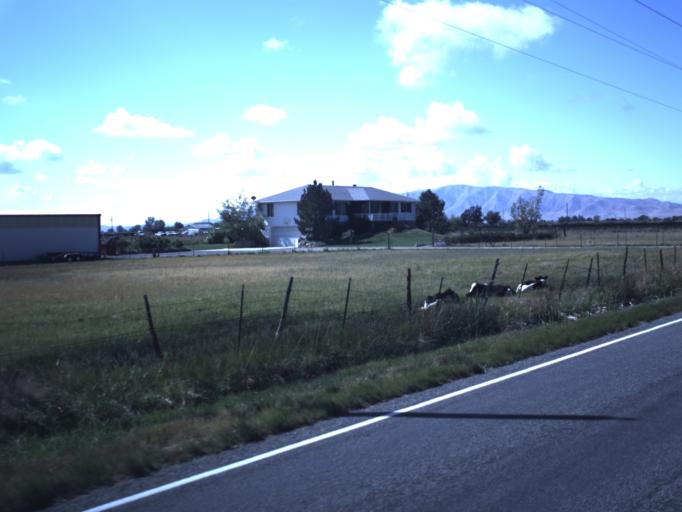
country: US
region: Utah
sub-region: Utah County
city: Spanish Fork
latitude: 40.1586
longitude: -111.6701
